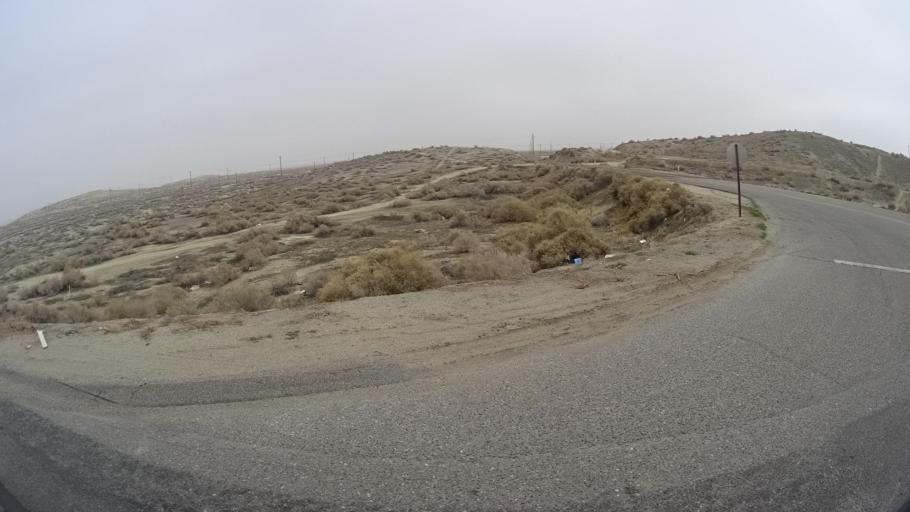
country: US
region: California
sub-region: Kern County
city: Maricopa
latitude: 35.0840
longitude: -119.4018
